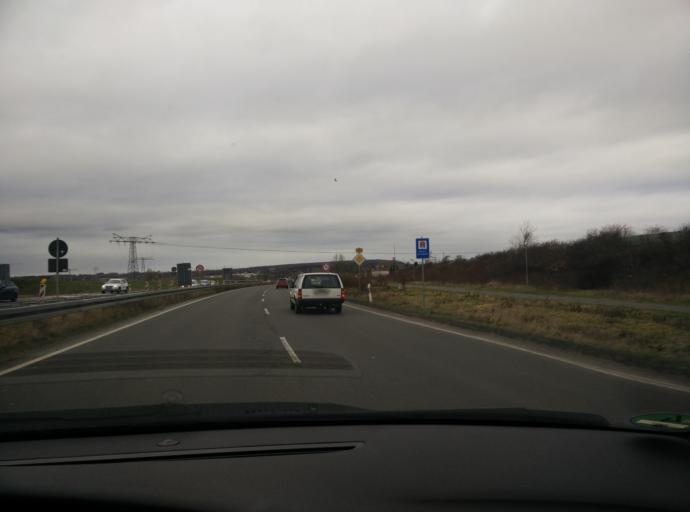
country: DE
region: Saxony
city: Borna
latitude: 51.1378
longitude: 12.5102
